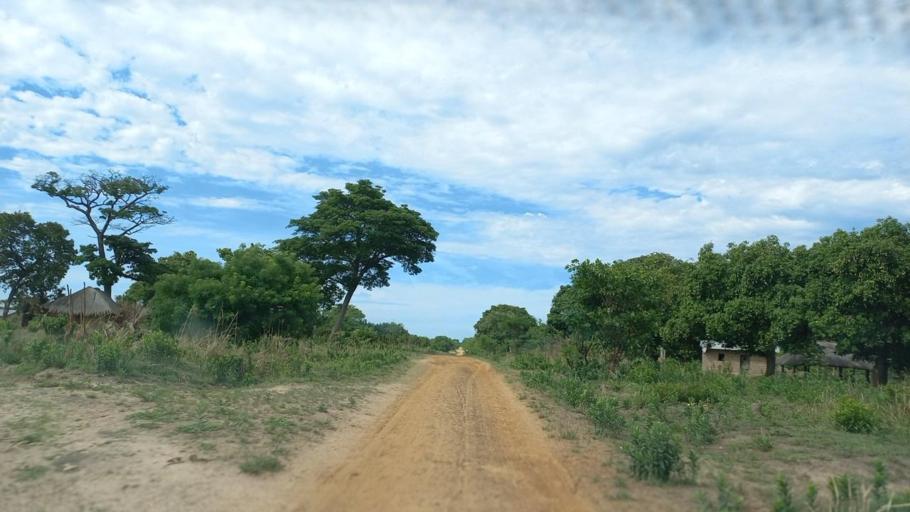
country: ZM
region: North-Western
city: Kabompo
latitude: -13.5142
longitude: 24.3905
